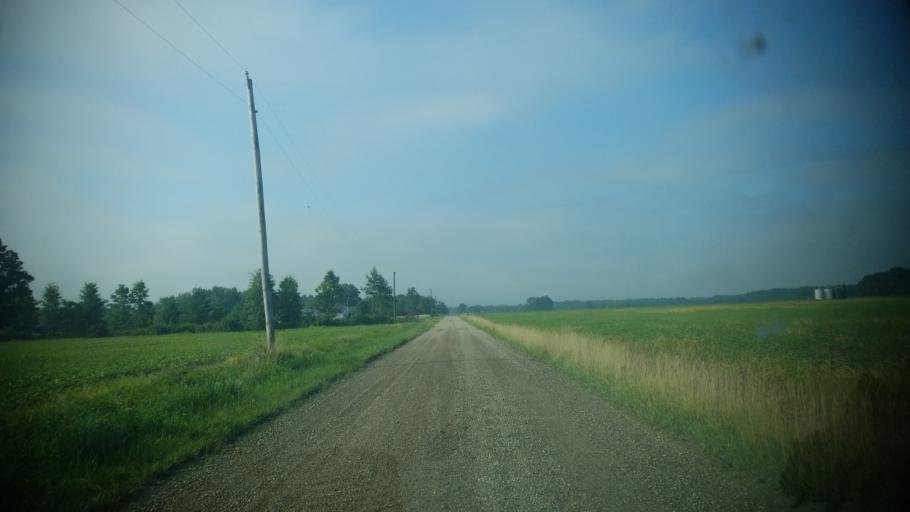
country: US
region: Illinois
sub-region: Clay County
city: Flora
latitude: 38.5982
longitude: -88.3643
